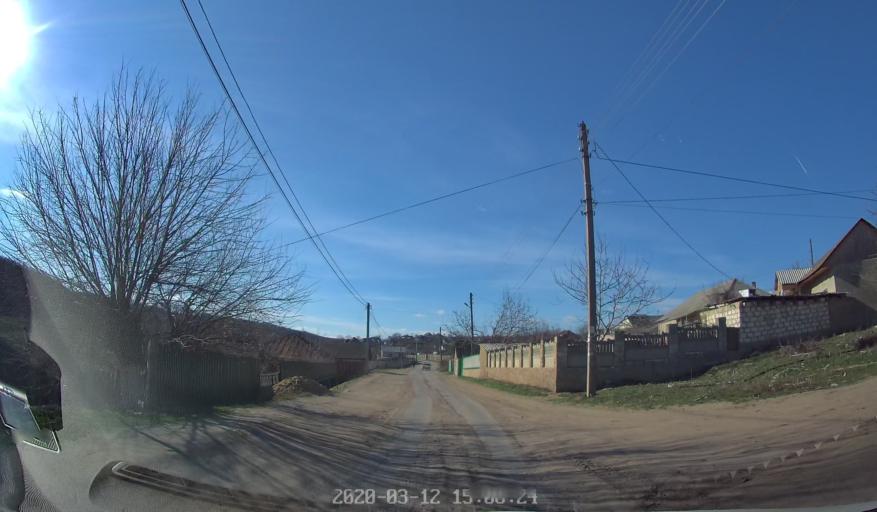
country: MD
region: Chisinau
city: Ciorescu
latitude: 47.2217
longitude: 28.9935
